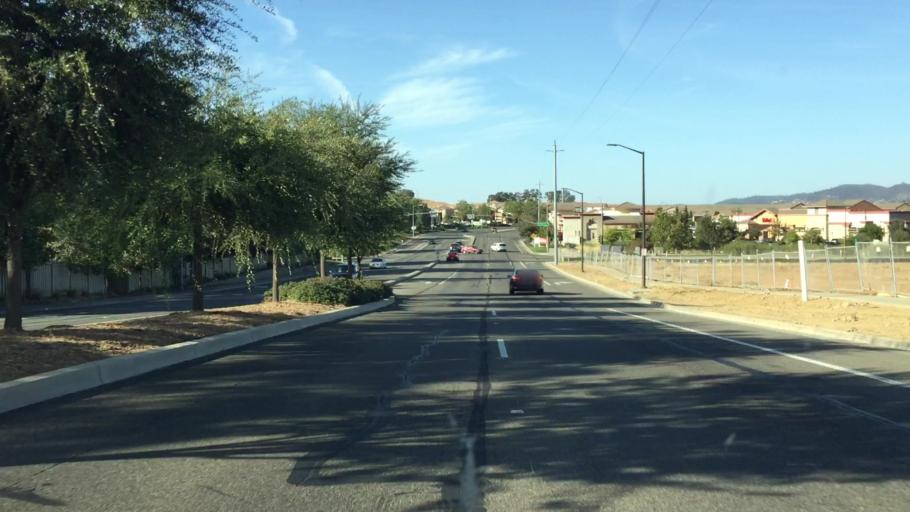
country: US
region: California
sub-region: El Dorado County
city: El Dorado Hills
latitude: 38.6864
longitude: -121.1240
